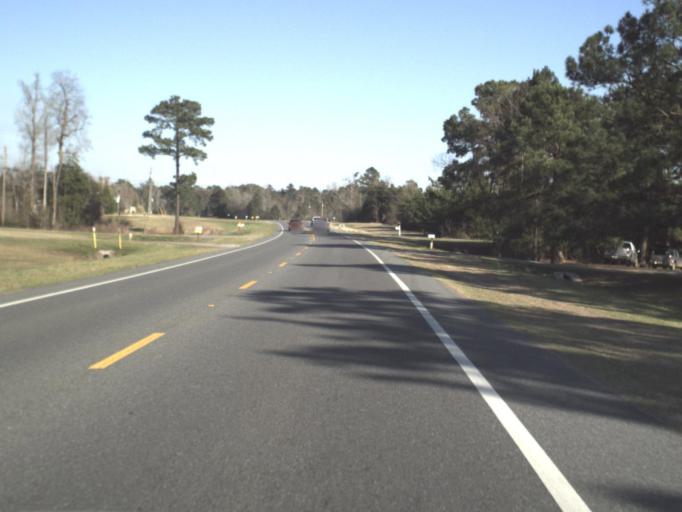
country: US
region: Florida
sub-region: Jackson County
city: Marianna
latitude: 30.7402
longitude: -85.1446
